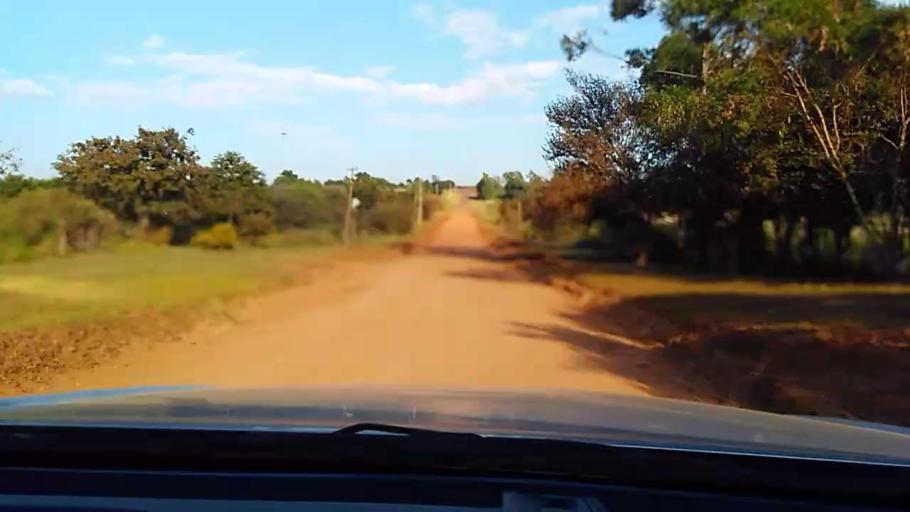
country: PY
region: Alto Parana
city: Santa Rita
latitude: -25.7066
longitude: -55.3843
